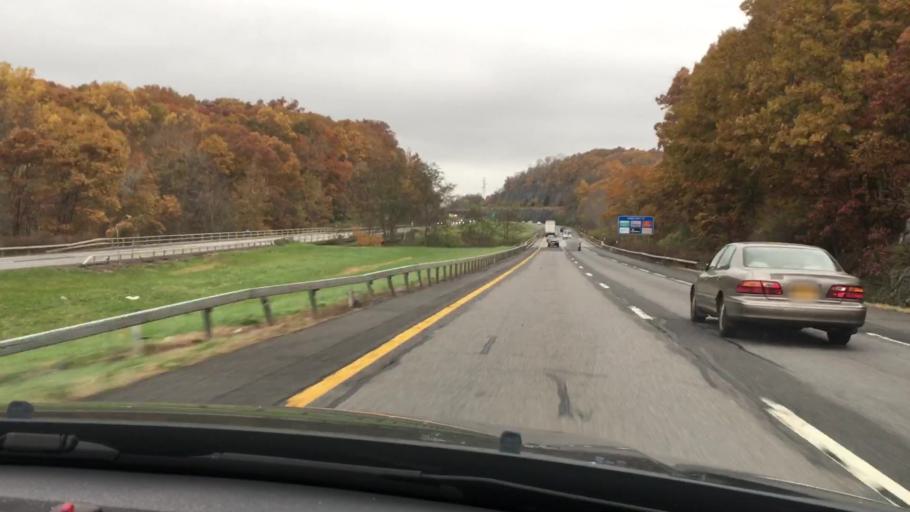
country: US
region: New York
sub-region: Putnam County
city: Brewster Hill
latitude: 41.4183
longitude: -73.6215
